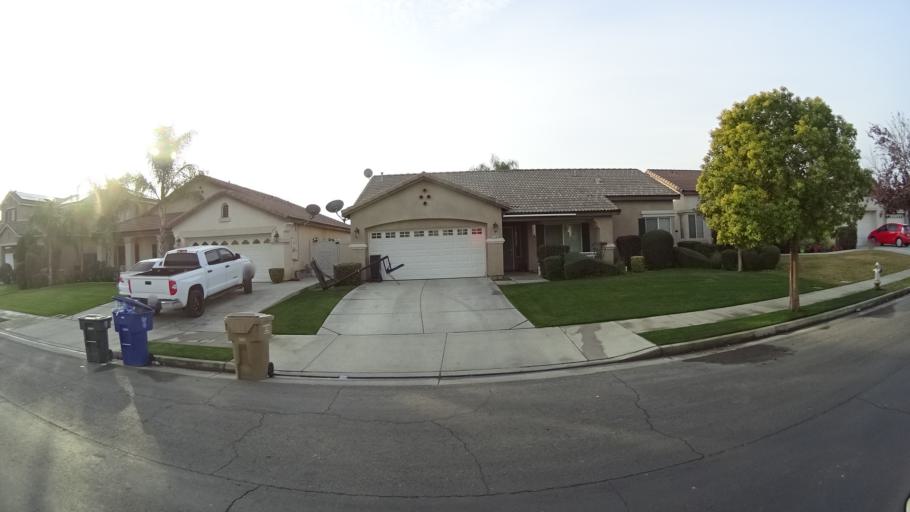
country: US
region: California
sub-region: Kern County
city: Greenacres
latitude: 35.4229
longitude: -119.1254
